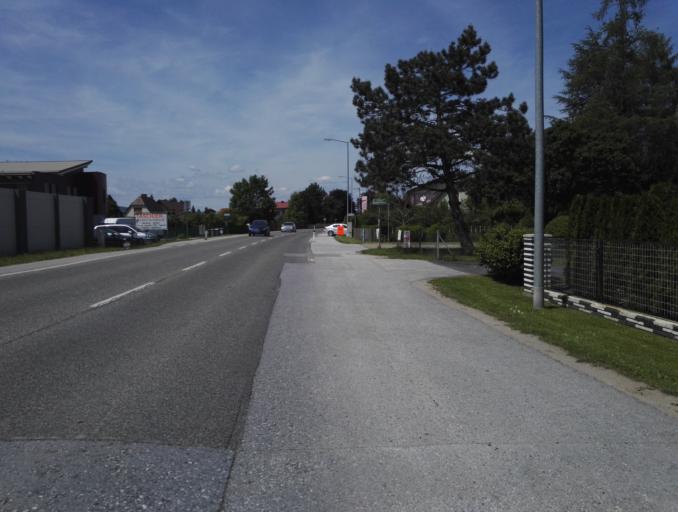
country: AT
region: Styria
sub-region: Politischer Bezirk Graz-Umgebung
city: Gossendorf
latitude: 46.9873
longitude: 15.4583
